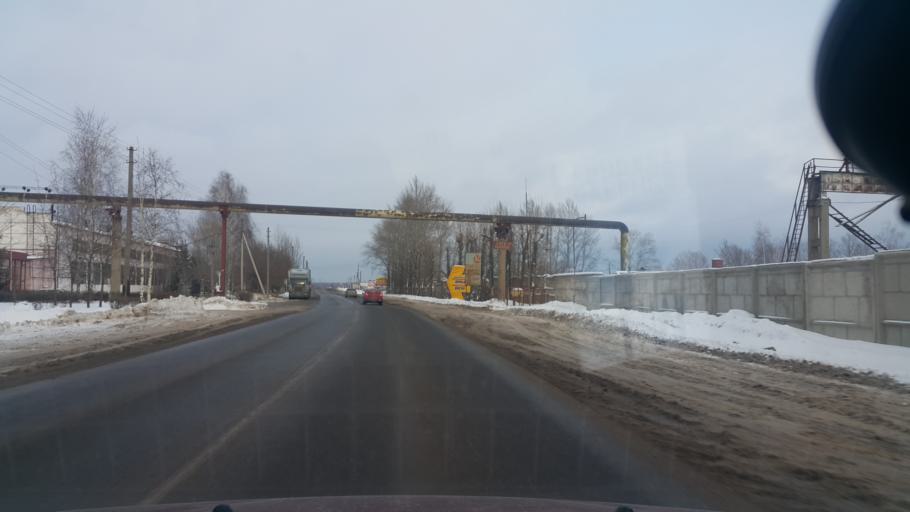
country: RU
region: Tambov
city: Pokrovo-Prigorodnoye
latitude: 52.6572
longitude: 41.4287
